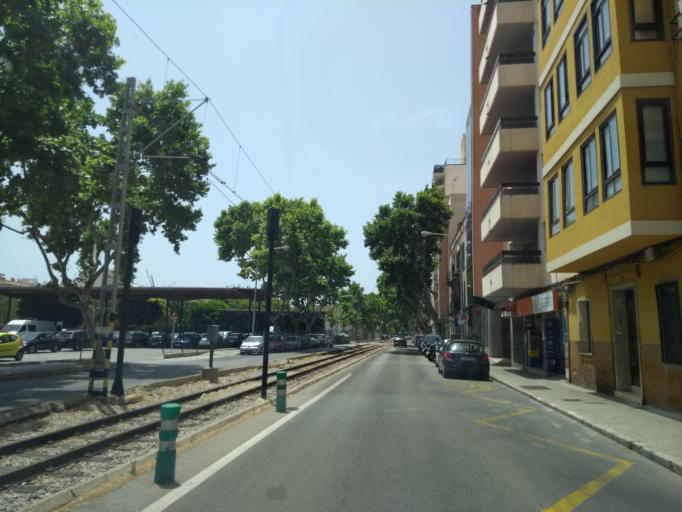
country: ES
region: Balearic Islands
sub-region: Illes Balears
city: Palma
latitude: 39.5793
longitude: 2.6577
